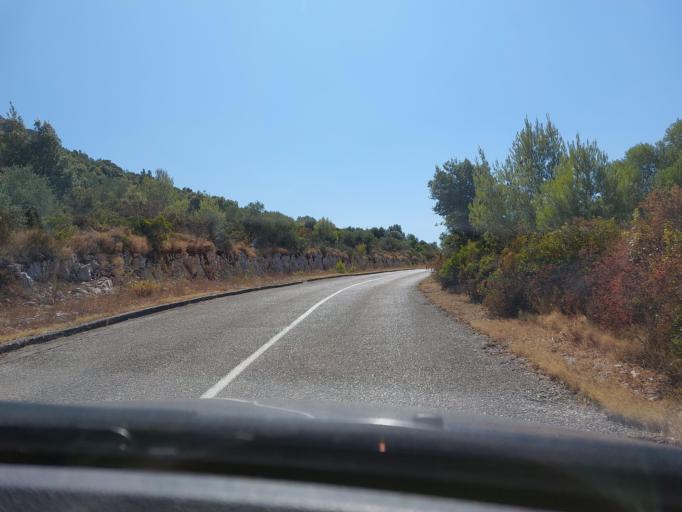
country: HR
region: Dubrovacko-Neretvanska
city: Smokvica
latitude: 42.7478
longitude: 16.8778
